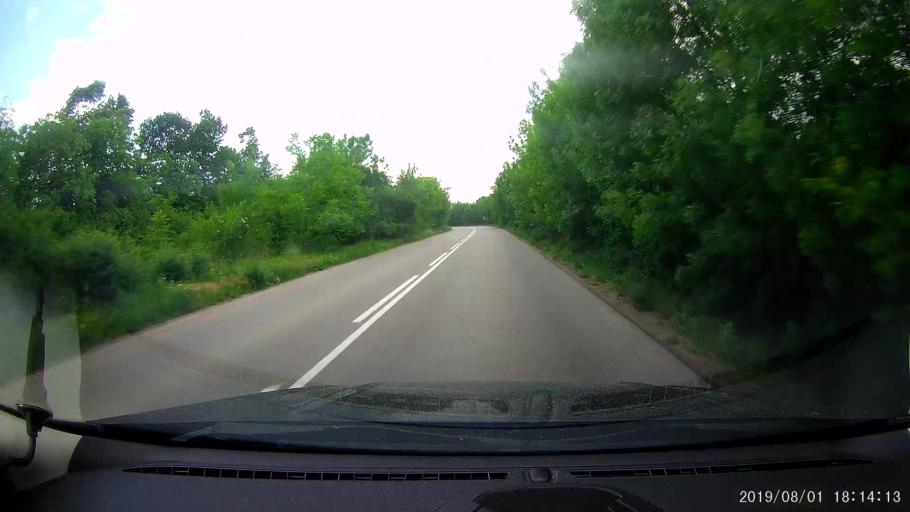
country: BG
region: Silistra
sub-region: Obshtina Dulovo
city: Dulovo
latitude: 43.7736
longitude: 27.1272
